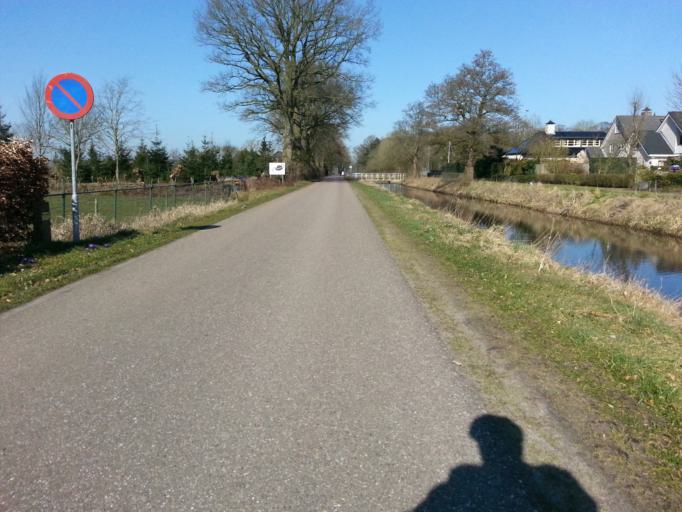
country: NL
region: Utrecht
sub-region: Gemeente Woudenberg
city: Woudenberg
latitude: 52.0864
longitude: 5.4022
